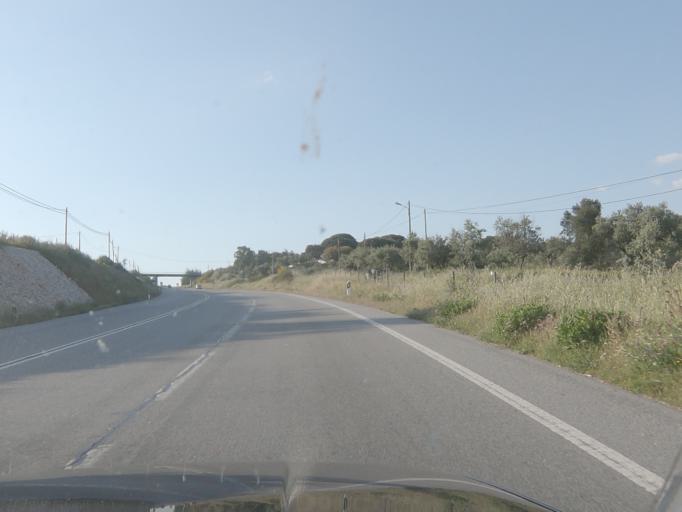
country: PT
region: Portalegre
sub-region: Portalegre
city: Portalegre
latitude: 39.3026
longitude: -7.4395
